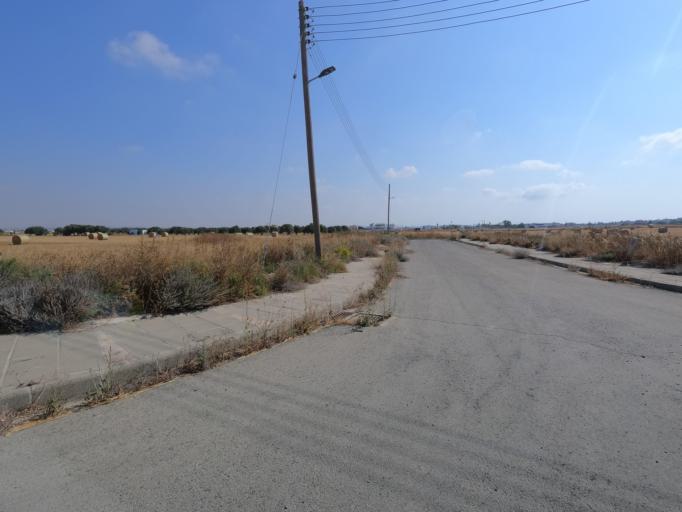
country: CY
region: Larnaka
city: Dhromolaxia
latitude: 34.8806
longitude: 33.5789
